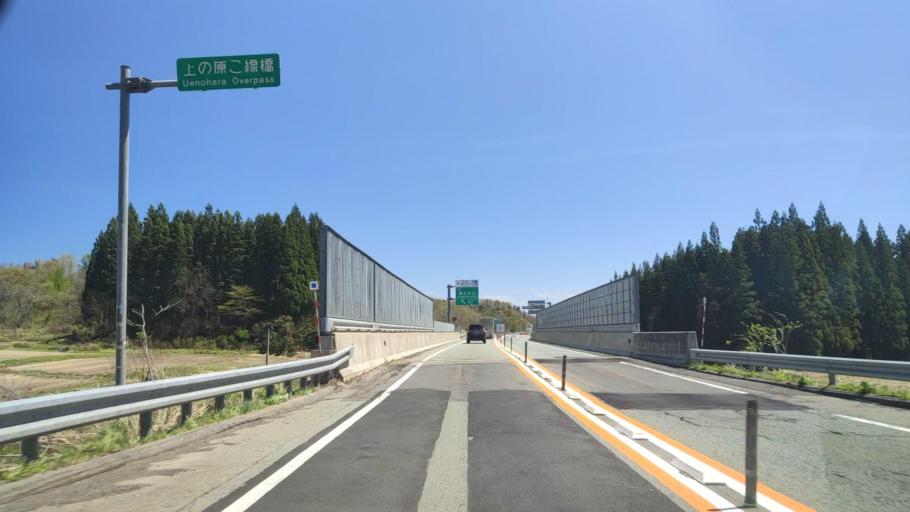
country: JP
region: Yamagata
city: Obanazawa
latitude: 38.6620
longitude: 140.3600
